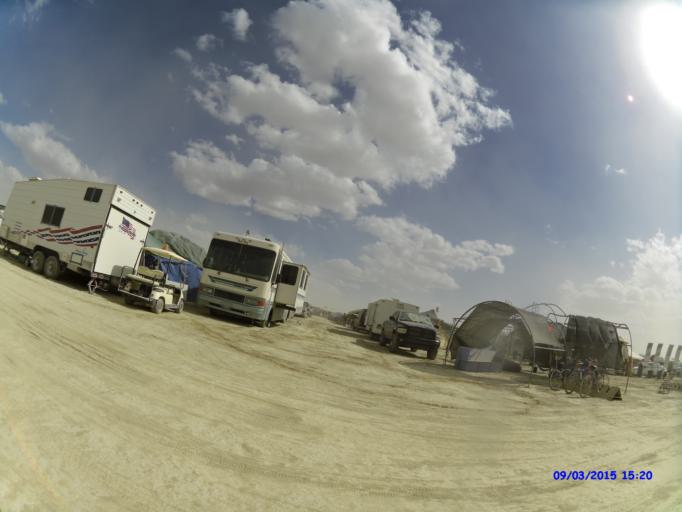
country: US
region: Nevada
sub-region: Pershing County
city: Lovelock
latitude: 40.7786
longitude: -119.2013
